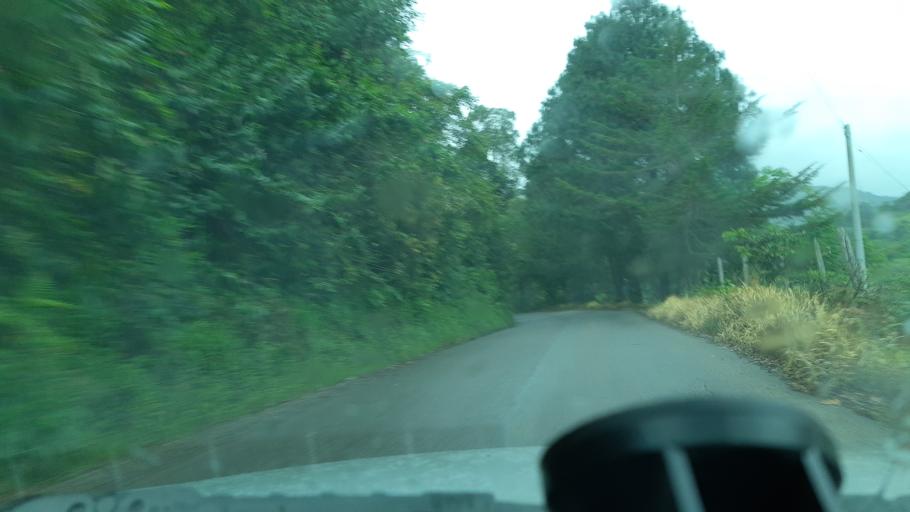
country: CO
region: Boyaca
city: Chinavita
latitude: 5.1947
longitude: -73.3820
